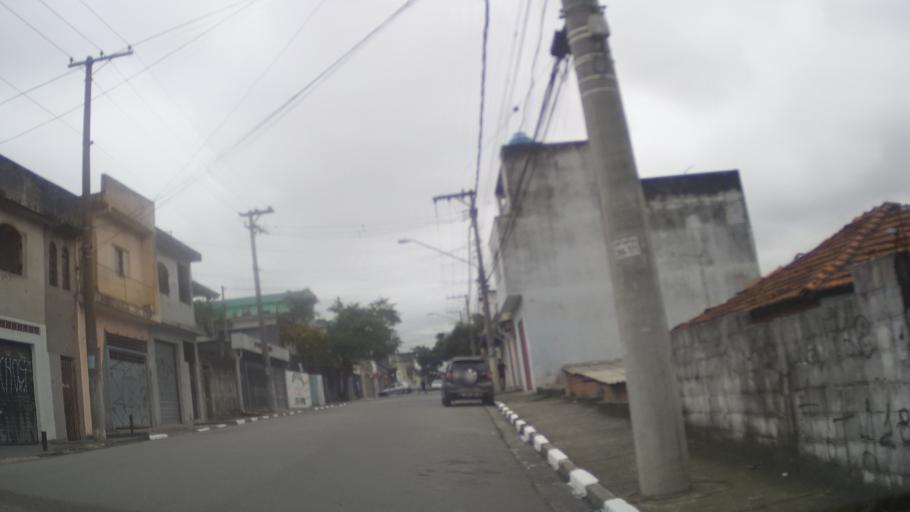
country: BR
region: Sao Paulo
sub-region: Guarulhos
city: Guarulhos
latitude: -23.4421
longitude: -46.5159
